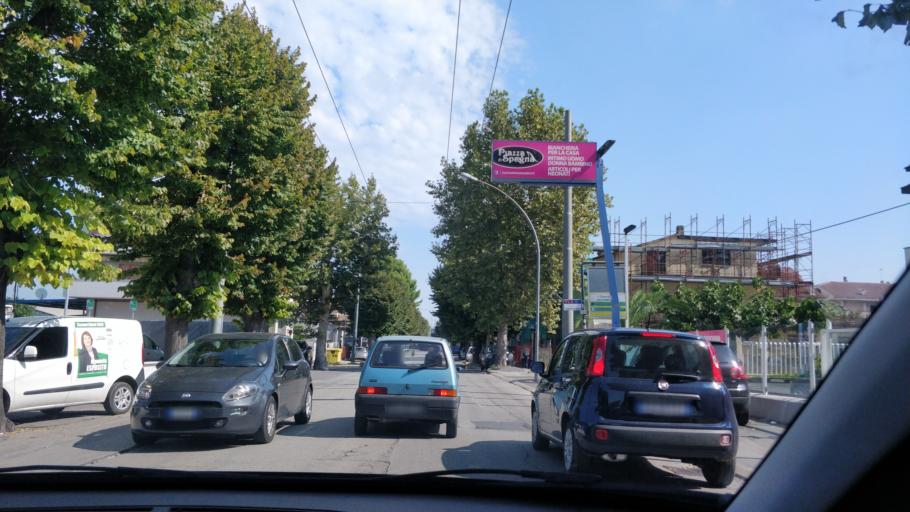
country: IT
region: Abruzzo
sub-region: Provincia di Chieti
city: Chieti
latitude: 42.3773
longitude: 14.1466
